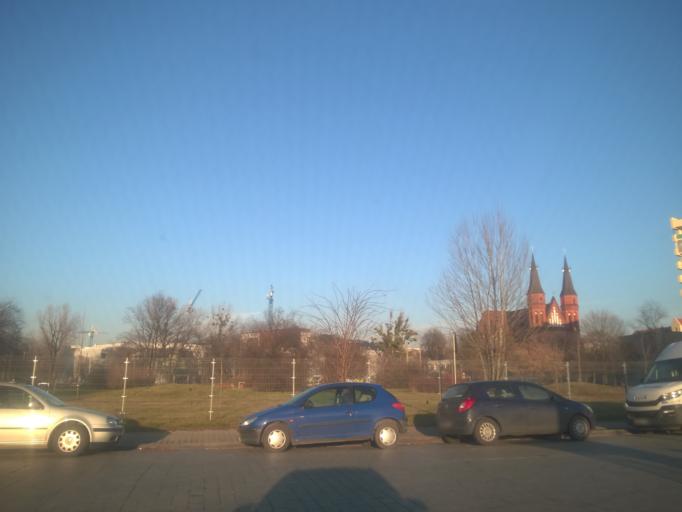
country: PL
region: Lower Silesian Voivodeship
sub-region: Powiat wroclawski
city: Wroclaw
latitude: 51.0932
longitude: 17.0321
